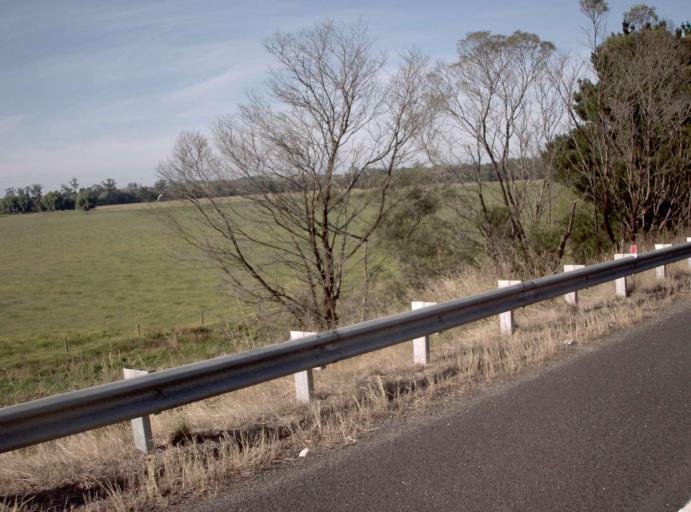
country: AU
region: Victoria
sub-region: East Gippsland
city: Lakes Entrance
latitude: -37.7091
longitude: 148.4645
